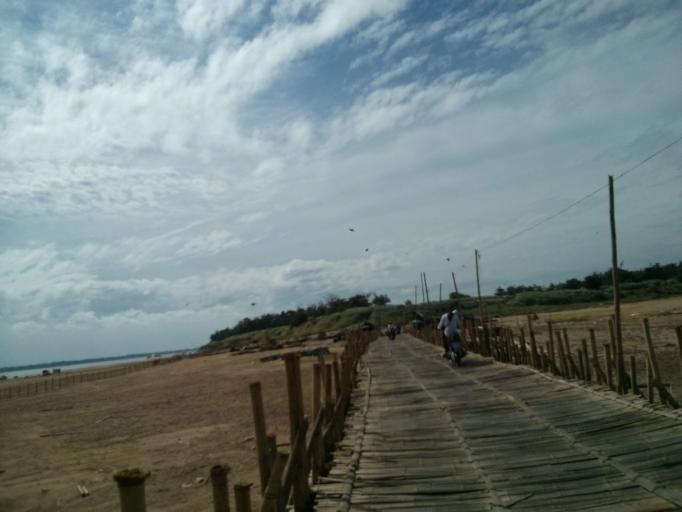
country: KH
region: Kampong Cham
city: Kampong Cham
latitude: 11.9713
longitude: 105.4629
